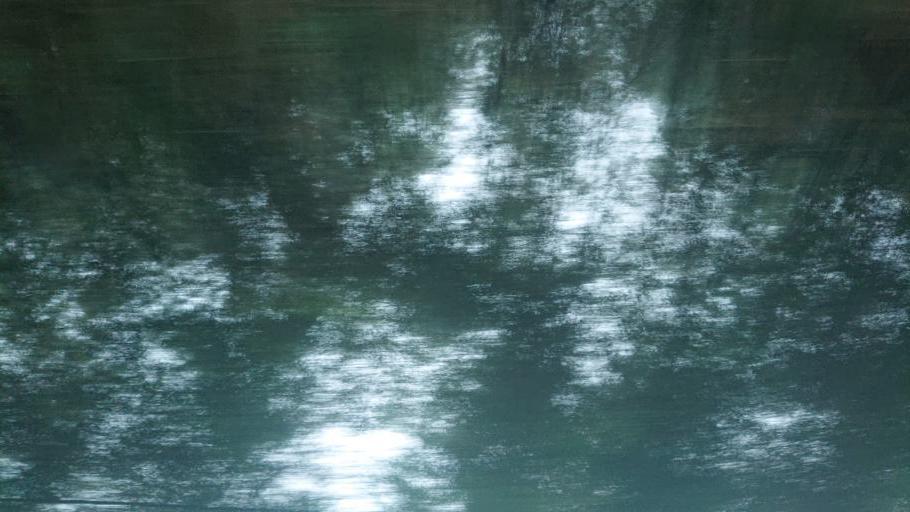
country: TW
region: Taiwan
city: Lugu
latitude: 23.5067
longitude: 120.7028
